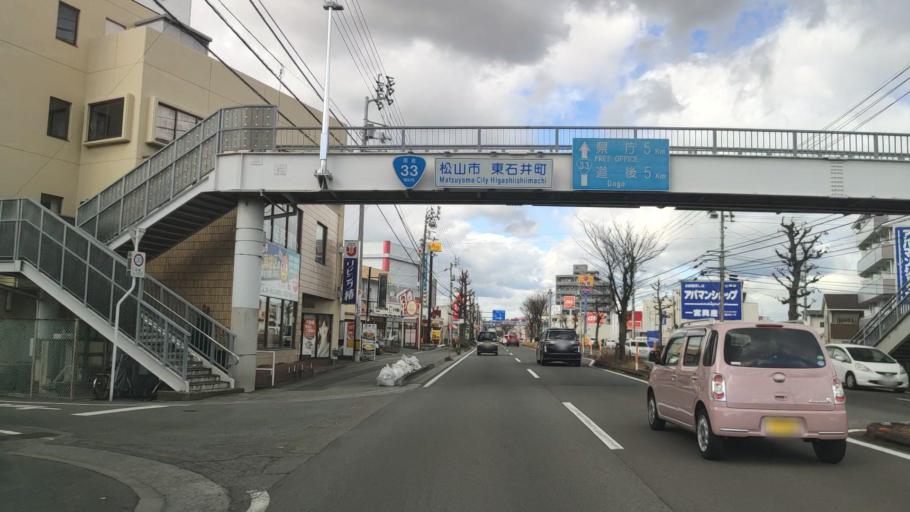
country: JP
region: Ehime
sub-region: Shikoku-chuo Shi
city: Matsuyama
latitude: 33.8102
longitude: 132.7796
